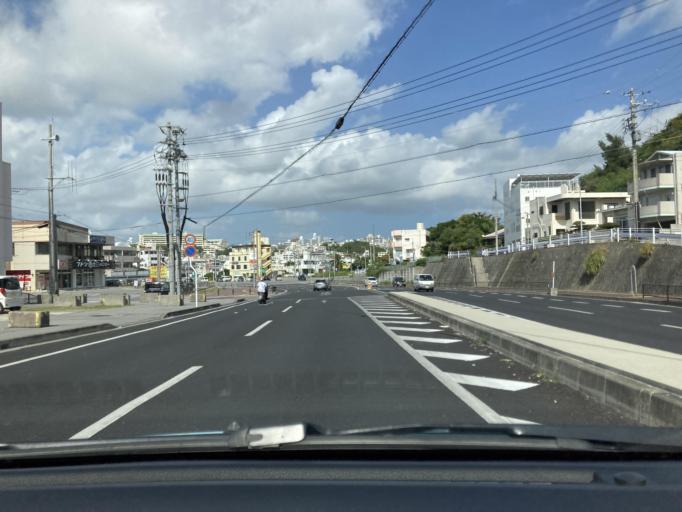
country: JP
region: Okinawa
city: Tomigusuku
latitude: 26.1925
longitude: 127.6942
